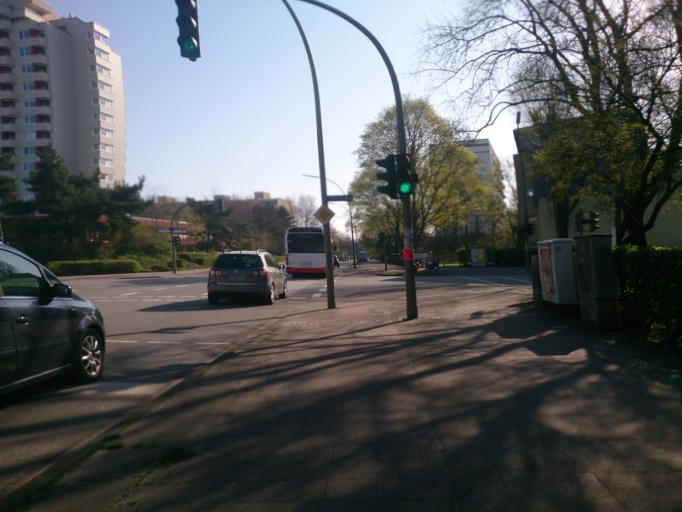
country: DE
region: Lower Saxony
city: Neu Wulmstorf
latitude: 53.4772
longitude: 9.8746
